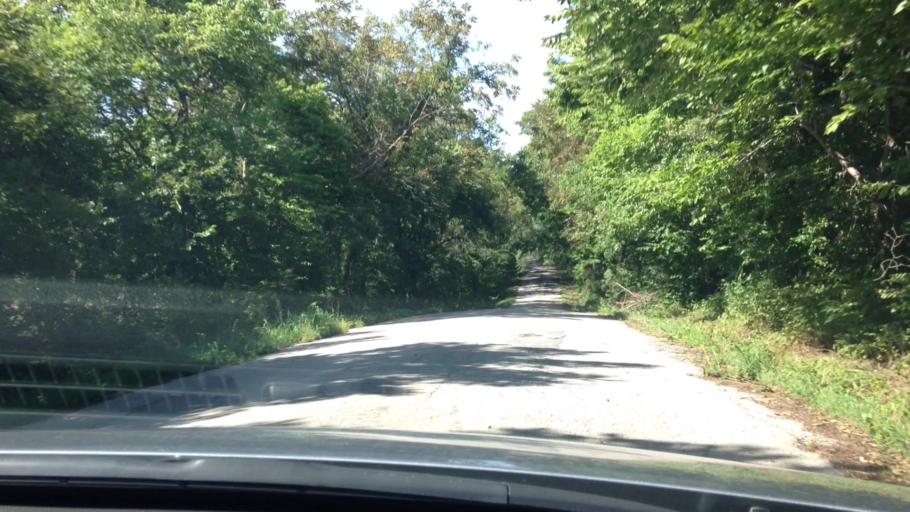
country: US
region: Missouri
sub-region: Platte County
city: Weatherby Lake
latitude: 39.3283
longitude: -94.6676
